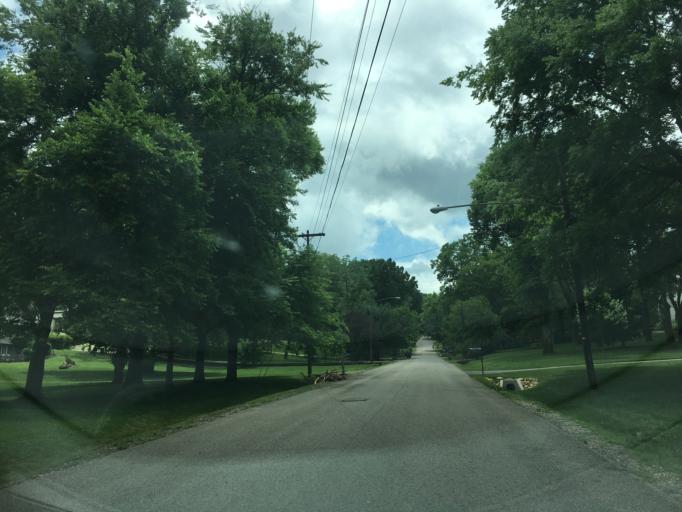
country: US
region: Tennessee
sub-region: Davidson County
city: Belle Meade
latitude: 36.0902
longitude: -86.8459
